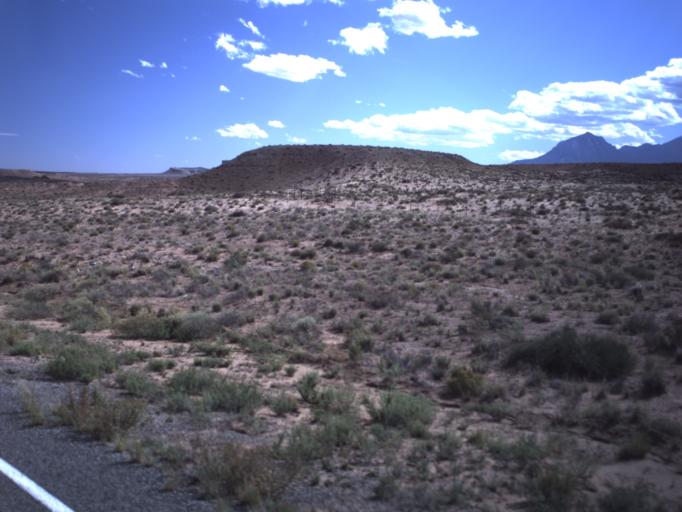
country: US
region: Utah
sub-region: Emery County
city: Ferron
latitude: 38.3339
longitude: -110.6831
